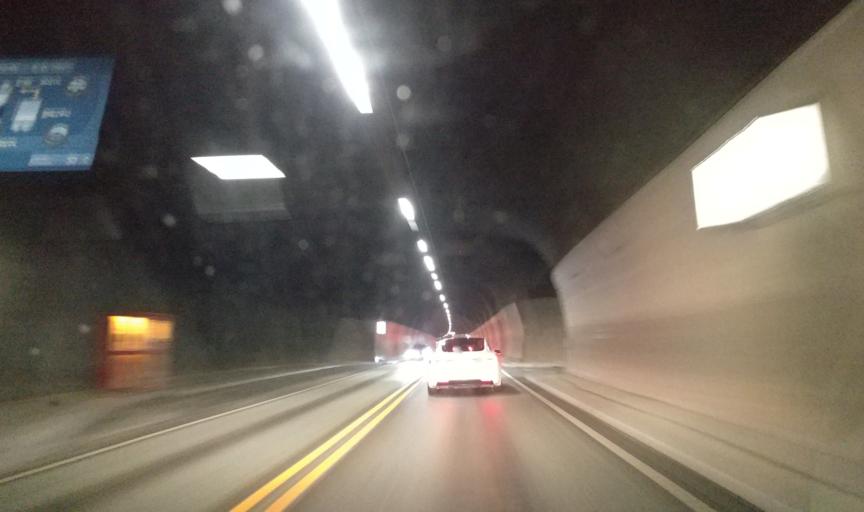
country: NO
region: Sor-Trondelag
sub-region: Malvik
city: Hommelvik
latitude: 63.4260
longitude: 10.8396
